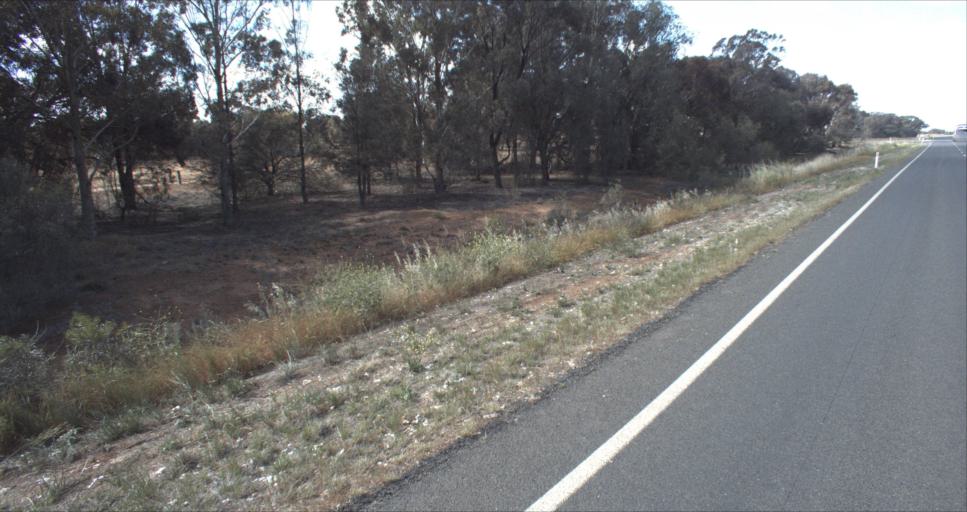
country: AU
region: New South Wales
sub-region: Murrumbidgee Shire
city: Darlington Point
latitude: -34.5394
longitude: 146.1724
